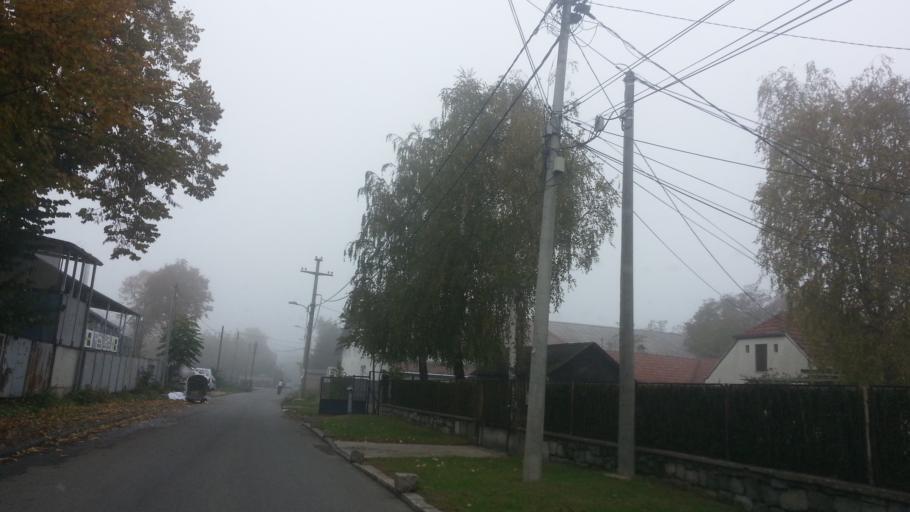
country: RS
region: Central Serbia
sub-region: Belgrade
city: Zemun
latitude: 44.8569
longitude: 20.3865
